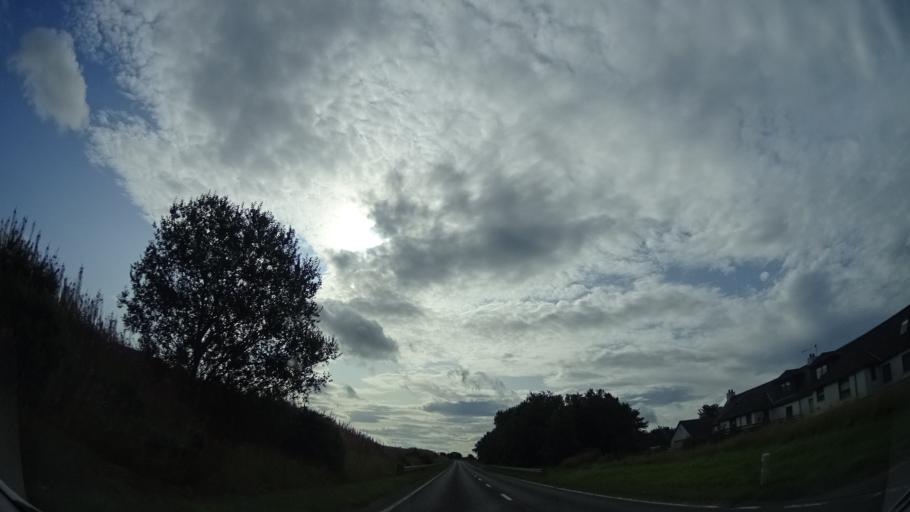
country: GB
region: Scotland
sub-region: Highland
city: Muir of Ord
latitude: 57.5604
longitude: -4.5527
